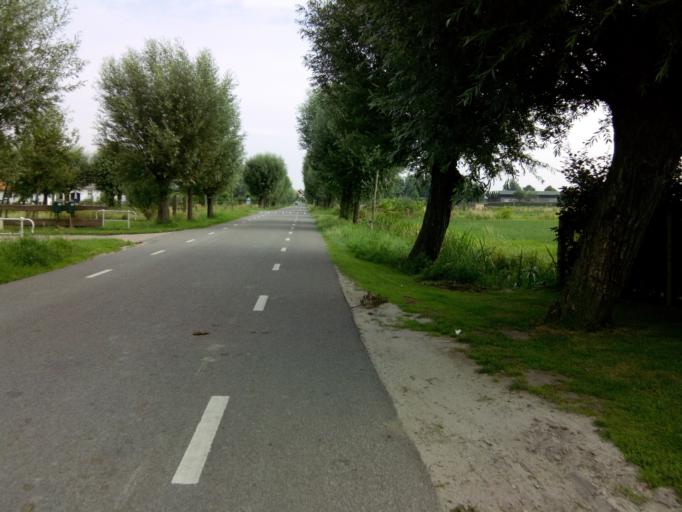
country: NL
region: Utrecht
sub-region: Gemeente Bunschoten
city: Spakenburg
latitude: 52.2579
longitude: 5.3331
